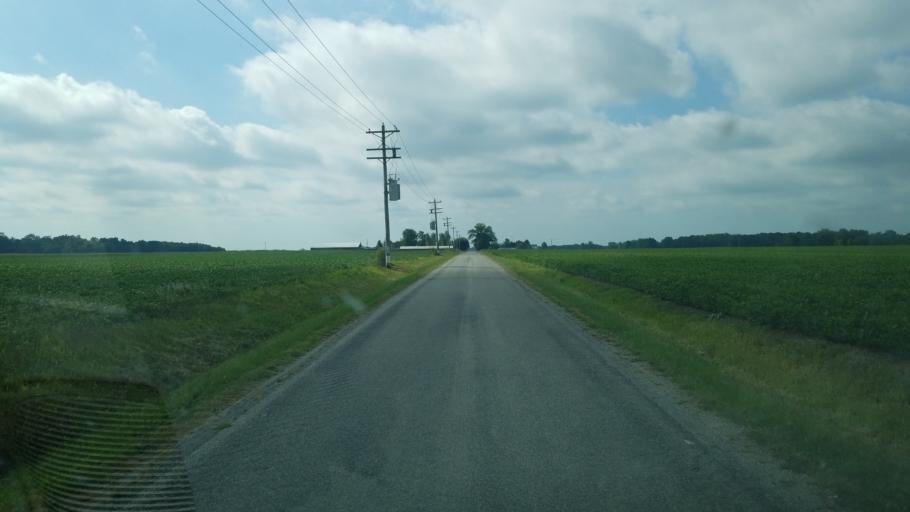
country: US
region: Ohio
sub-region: Union County
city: Richwood
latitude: 40.6054
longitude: -83.3617
